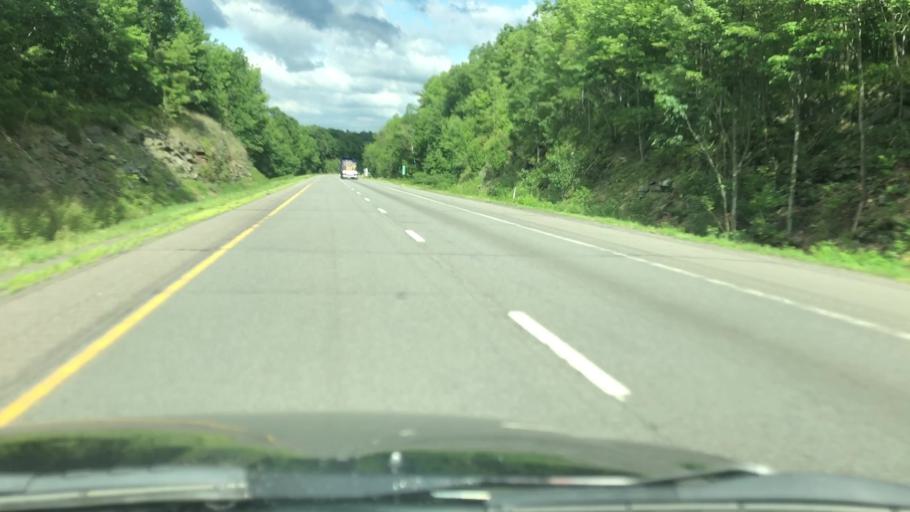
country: US
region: Pennsylvania
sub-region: Pike County
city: Hemlock Farms
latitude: 41.3668
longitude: -75.1396
